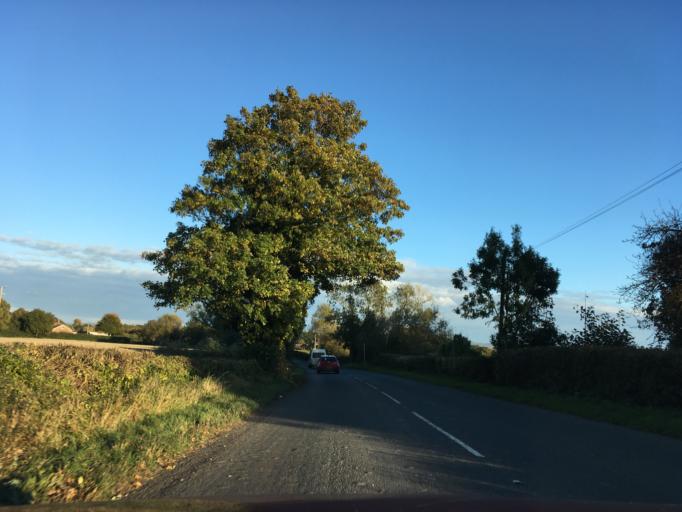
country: GB
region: England
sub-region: Gloucestershire
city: Tewkesbury
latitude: 52.0004
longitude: -2.1819
